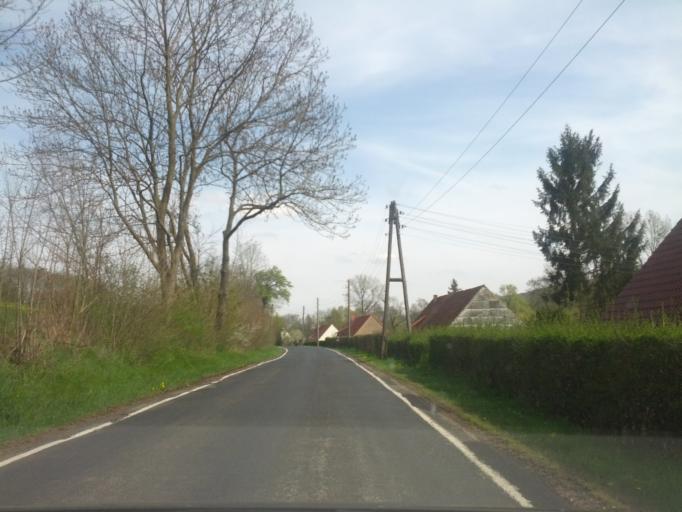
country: DE
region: Thuringia
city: Seebach
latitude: 50.9805
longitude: 10.4349
